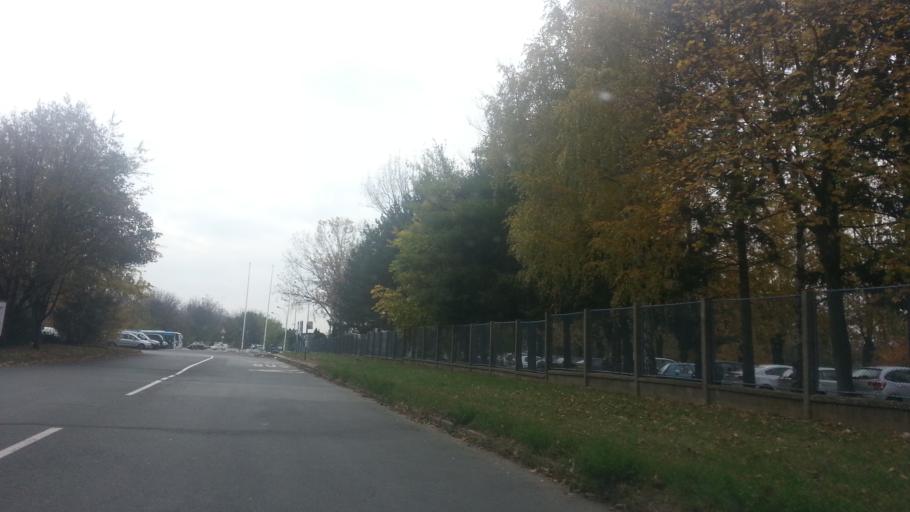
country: RS
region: Central Serbia
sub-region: Belgrade
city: Zemun
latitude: 44.8600
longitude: 20.3661
